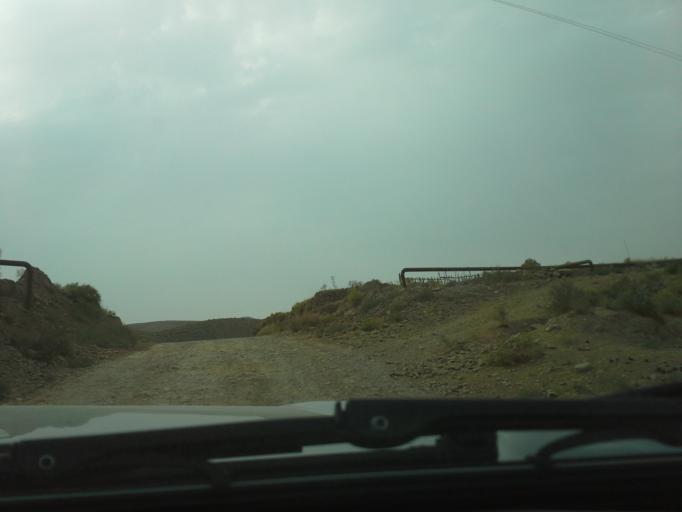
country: UZ
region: Qashqadaryo
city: Qorashina
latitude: 37.9336
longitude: 66.5075
